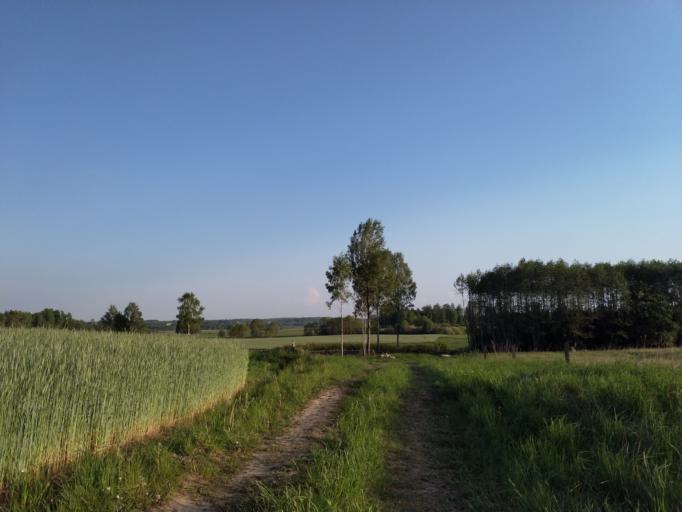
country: LV
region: Aizpute
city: Aizpute
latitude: 56.8306
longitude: 21.7822
